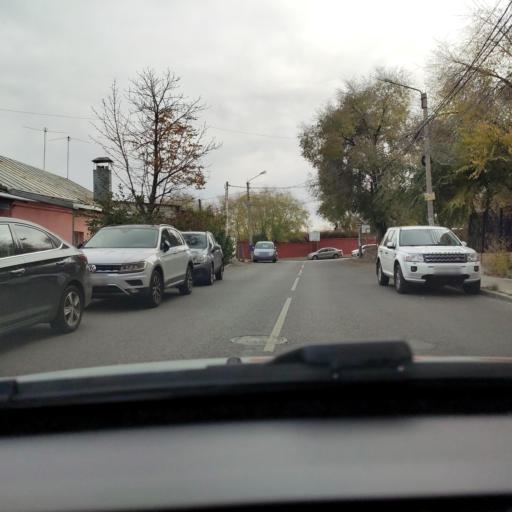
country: RU
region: Voronezj
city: Voronezh
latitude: 51.6658
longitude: 39.2146
